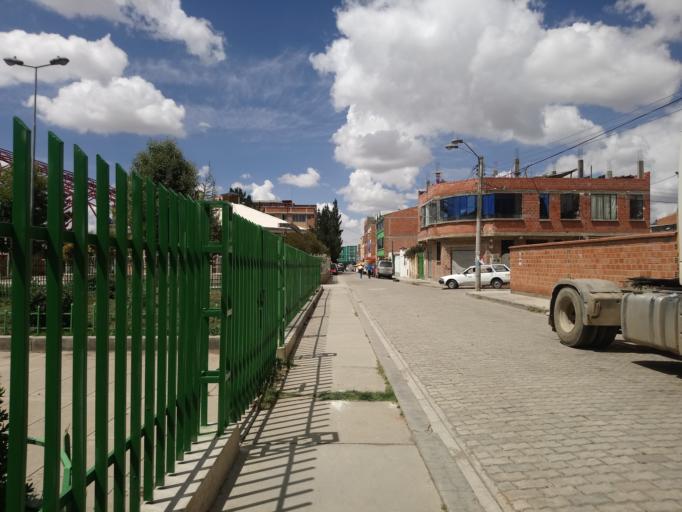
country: BO
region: La Paz
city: La Paz
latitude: -16.5564
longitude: -68.1923
